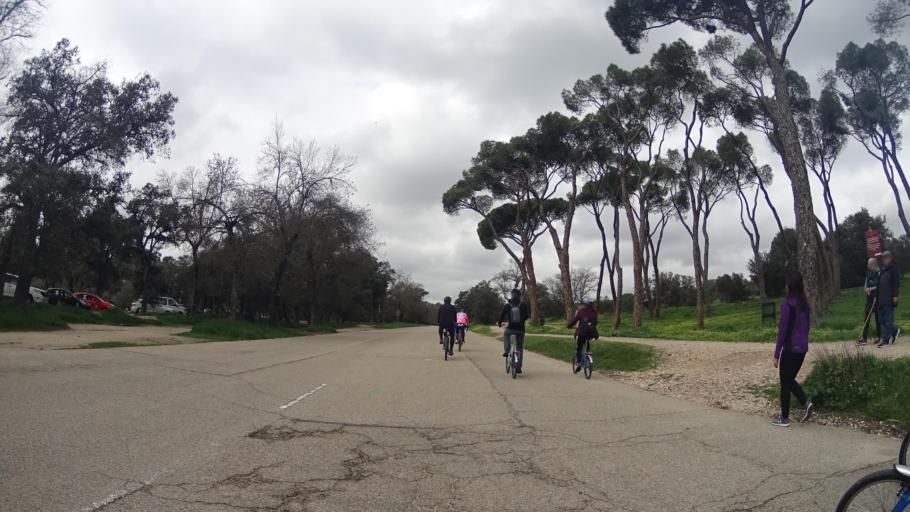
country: ES
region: Madrid
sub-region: Provincia de Madrid
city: Moncloa-Aravaca
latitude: 40.4159
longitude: -3.7482
